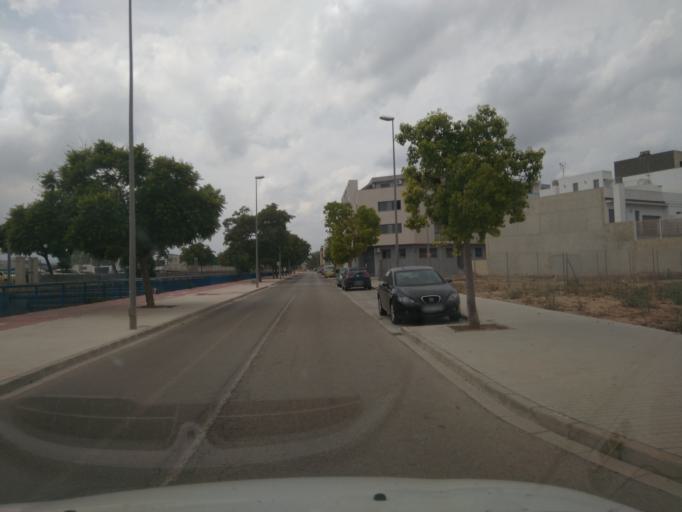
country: ES
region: Valencia
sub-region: Provincia de Valencia
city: L'Alcudia
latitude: 39.1909
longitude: -0.5026
